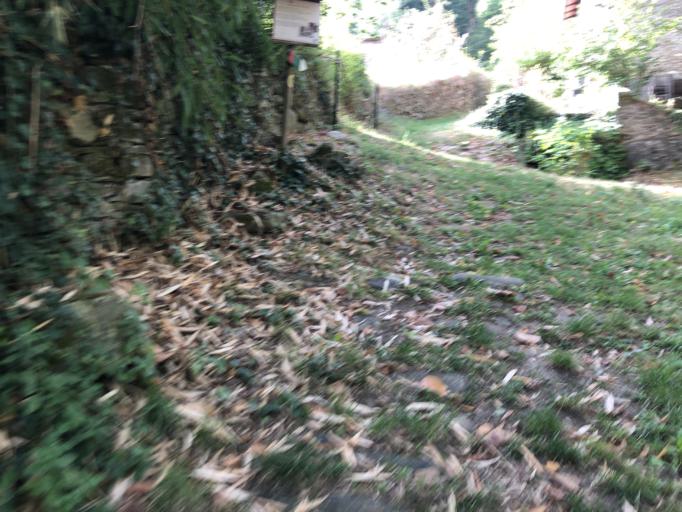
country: IT
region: Emilia-Romagna
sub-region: Forli-Cesena
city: Portico e San Benedetto
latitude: 44.0244
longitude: 11.7818
